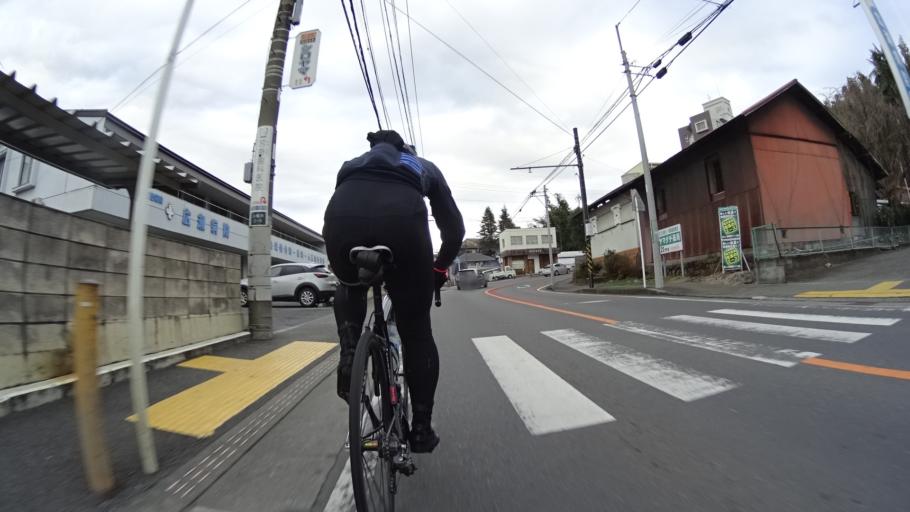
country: JP
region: Tokyo
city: Hachioji
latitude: 35.5936
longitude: 139.3004
